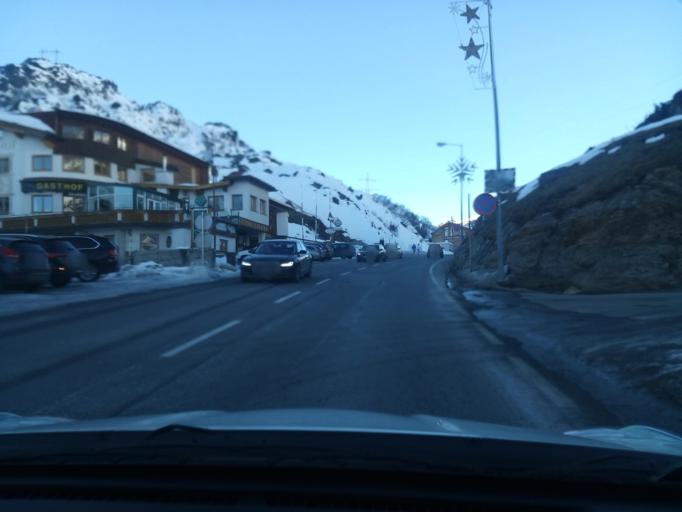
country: AT
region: Tyrol
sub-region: Politischer Bezirk Landeck
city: Sankt Anton am Arlberg
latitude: 47.1277
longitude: 10.2126
